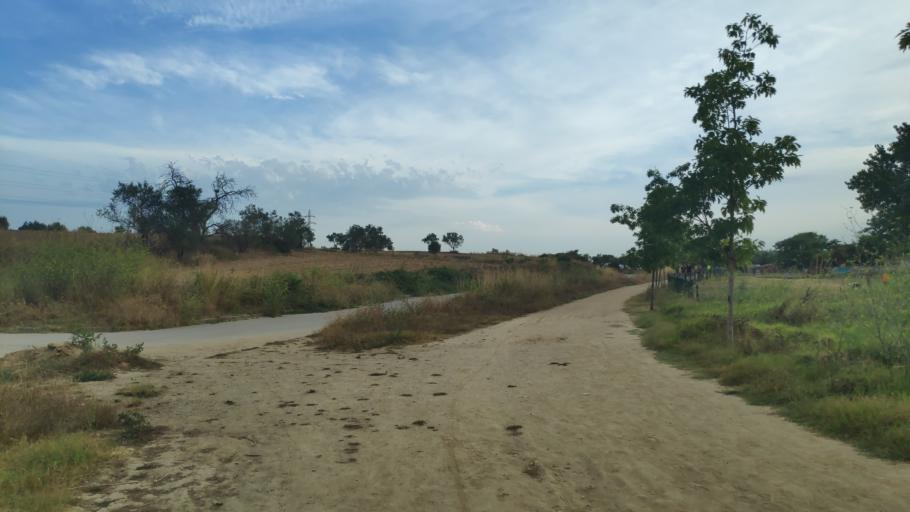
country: ES
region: Catalonia
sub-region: Provincia de Barcelona
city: Rubi
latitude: 41.4943
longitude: 2.0435
